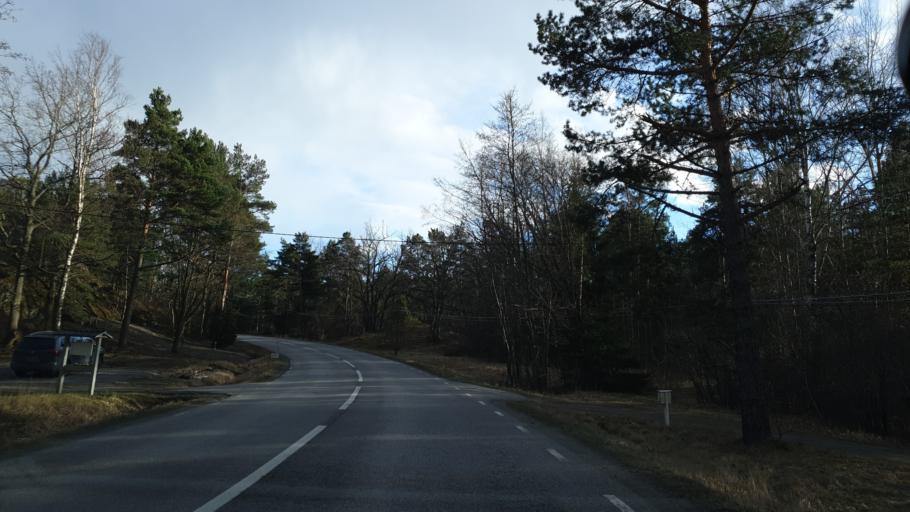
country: SE
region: Stockholm
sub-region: Varmdo Kommun
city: Holo
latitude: 59.3244
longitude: 18.7225
